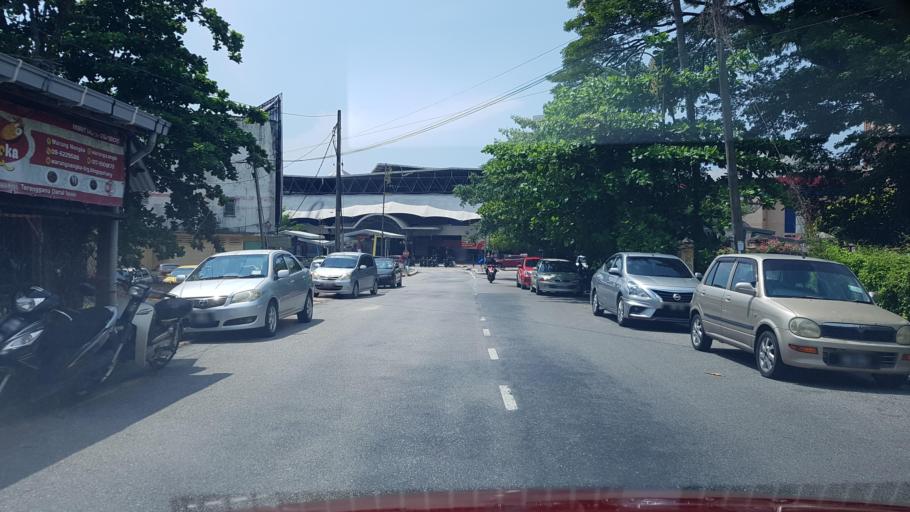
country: MY
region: Terengganu
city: Kuala Terengganu
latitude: 5.3327
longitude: 103.1360
